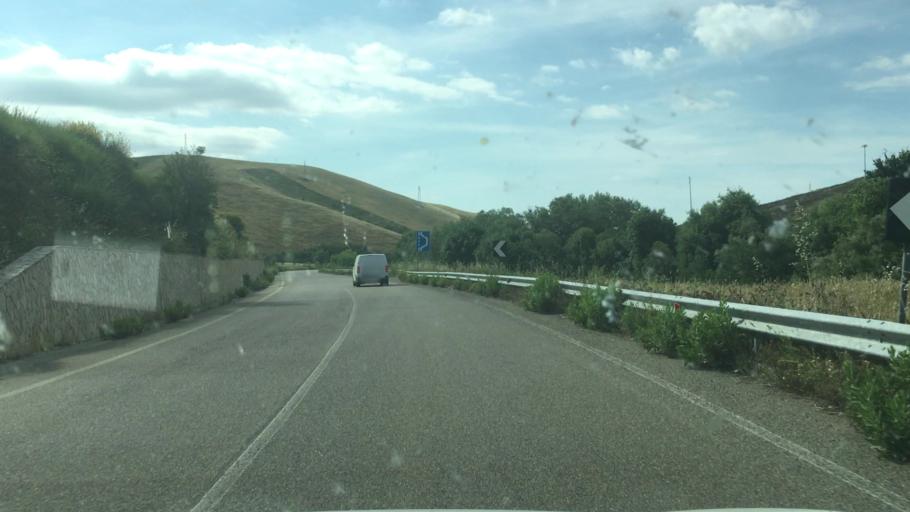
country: IT
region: Basilicate
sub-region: Provincia di Matera
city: Salandra
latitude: 40.5307
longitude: 16.2887
